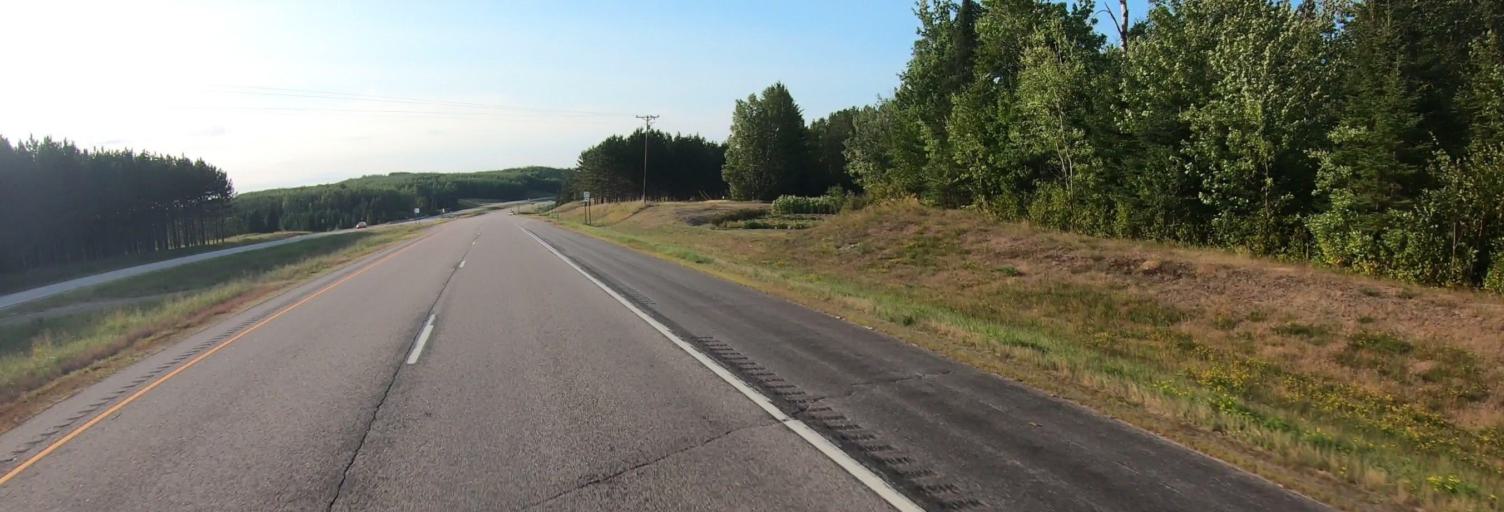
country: US
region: Minnesota
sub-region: Saint Louis County
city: Mountain Iron
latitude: 47.6758
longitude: -92.6344
